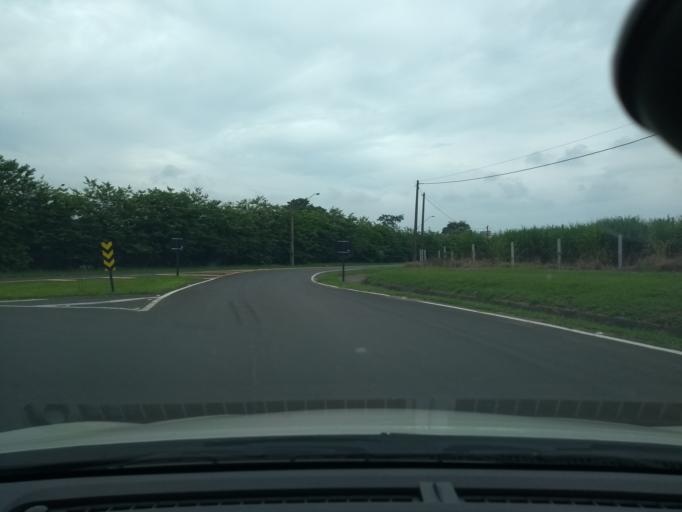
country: BR
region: Sao Paulo
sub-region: Rio Claro
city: Rio Claro
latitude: -22.3630
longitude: -47.5257
